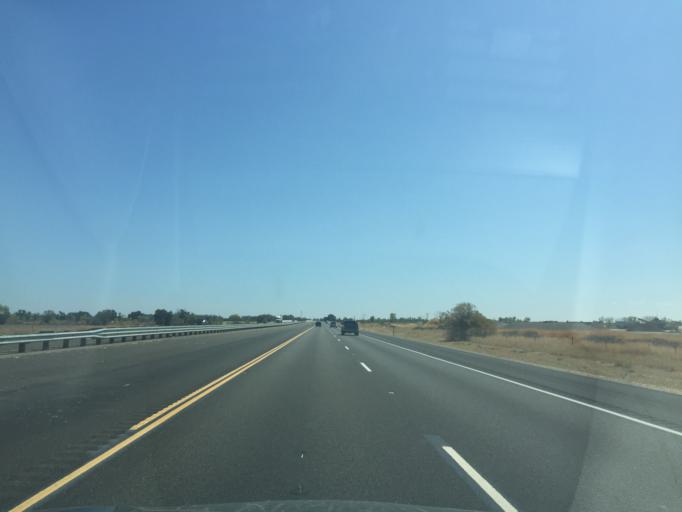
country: US
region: California
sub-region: Tehama County
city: Corning
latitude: 39.9809
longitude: -122.2028
